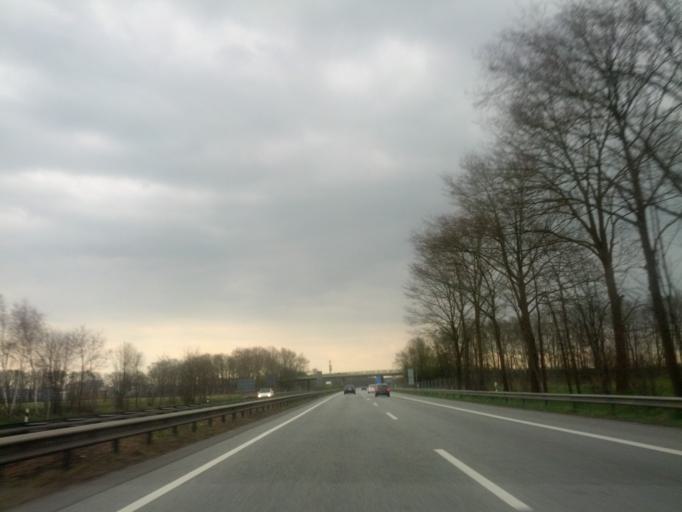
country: DE
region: Lower Saxony
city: Achim
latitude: 53.0214
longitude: 9.0499
